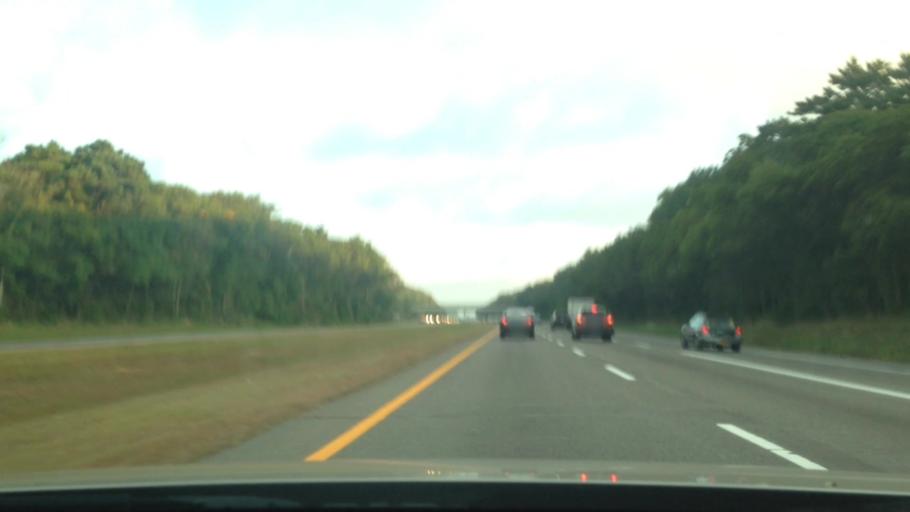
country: US
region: New York
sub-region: Suffolk County
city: Holtsville
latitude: 40.8222
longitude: -73.0544
